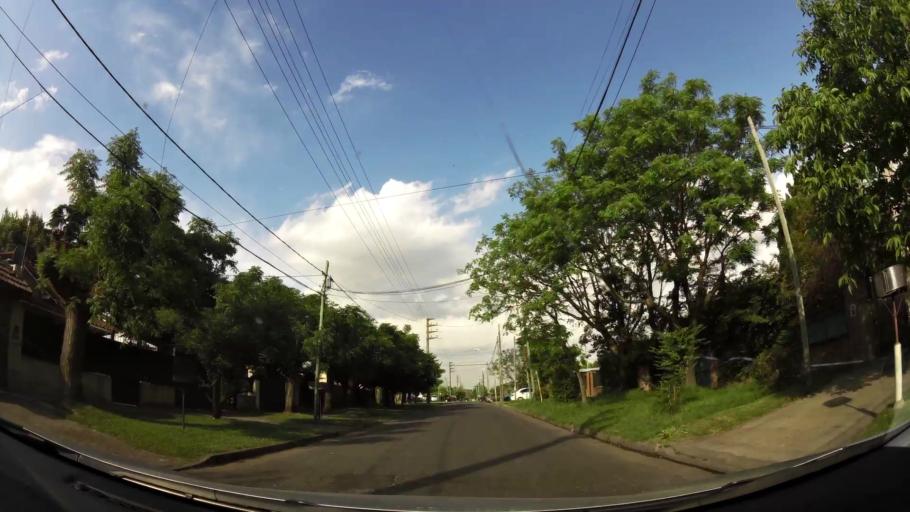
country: AR
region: Buenos Aires
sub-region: Partido de Tigre
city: Tigre
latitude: -34.4696
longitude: -58.6463
